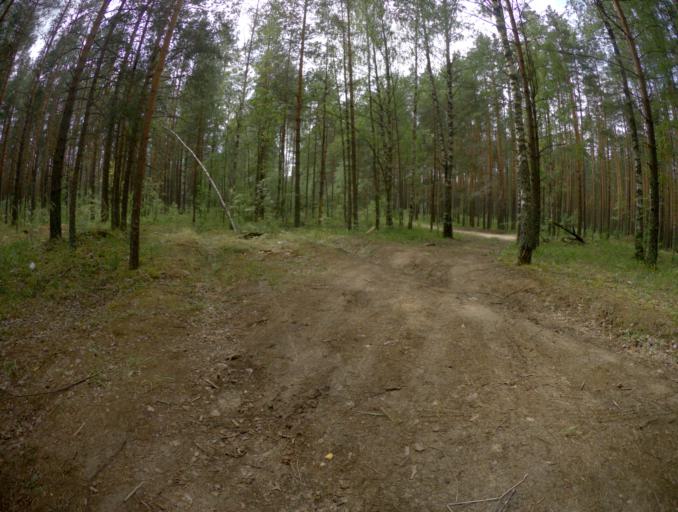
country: RU
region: Nizjnij Novgorod
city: Frolishchi
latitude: 56.3517
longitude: 42.7796
